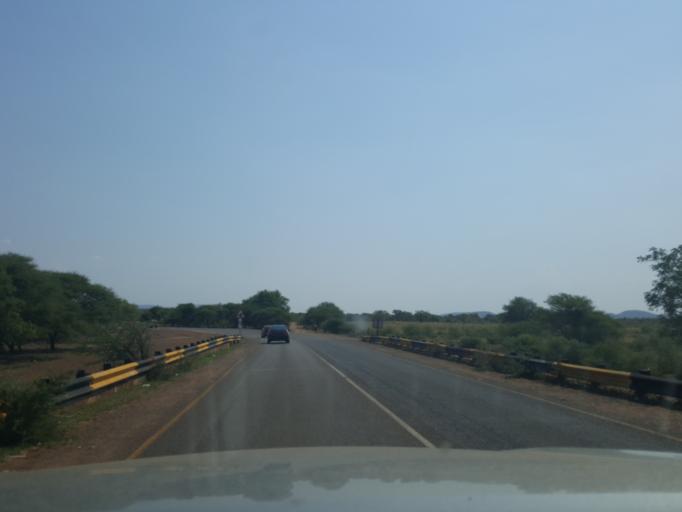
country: BW
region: South East
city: Ramotswa
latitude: -24.8507
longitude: 25.8291
